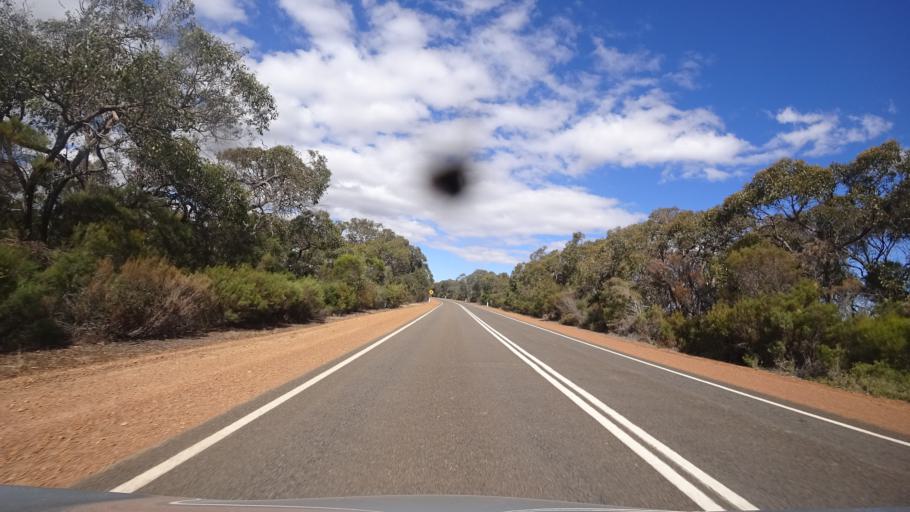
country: AU
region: South Australia
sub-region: Kangaroo Island
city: Kingscote
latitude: -35.7773
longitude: 137.3065
